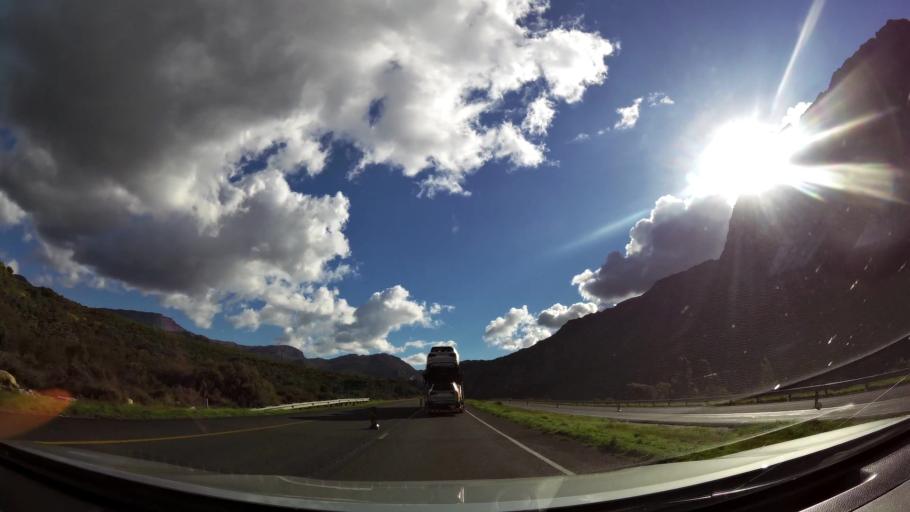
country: ZA
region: Western Cape
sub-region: Cape Winelands District Municipality
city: Paarl
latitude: -33.7248
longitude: 19.1509
